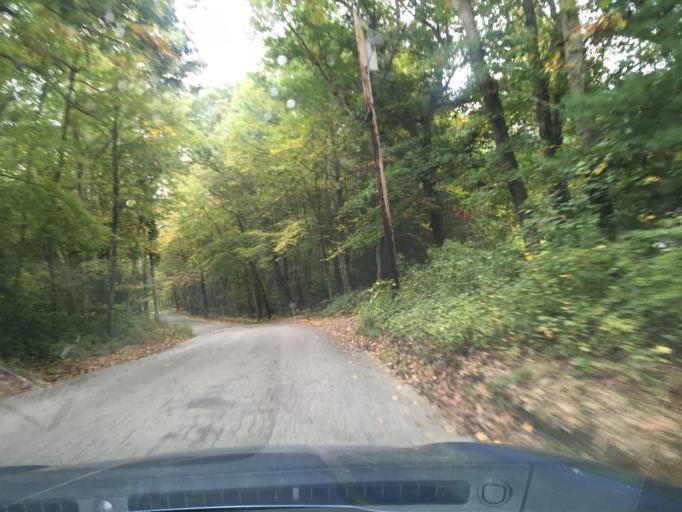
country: US
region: Rhode Island
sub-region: Washington County
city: Exeter
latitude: 41.6234
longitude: -71.5505
